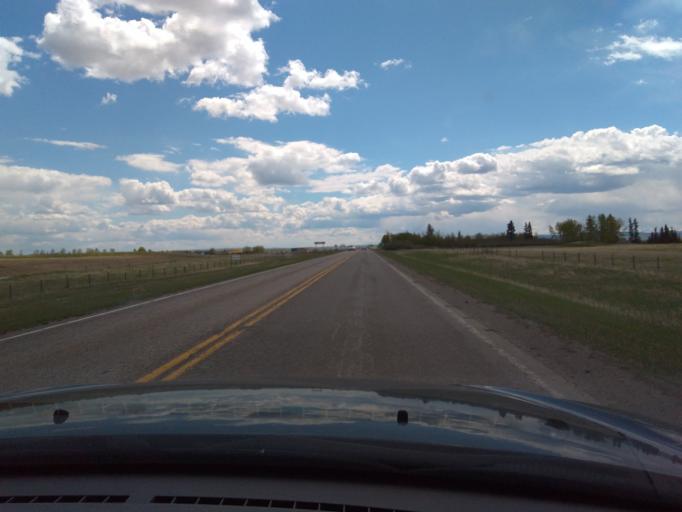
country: CA
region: Alberta
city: Cochrane
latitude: 51.0947
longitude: -114.3505
